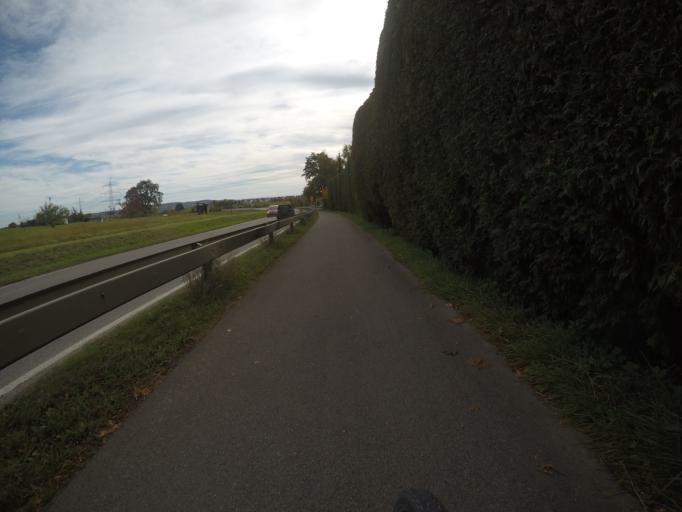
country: DE
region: Baden-Wuerttemberg
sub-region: Regierungsbezirk Stuttgart
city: Deckenpfronn
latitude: 48.6197
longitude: 8.8376
